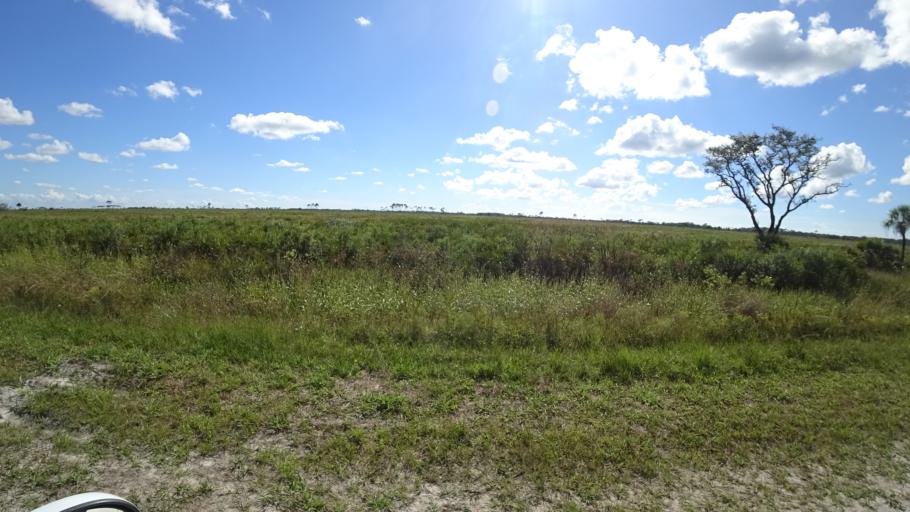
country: US
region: Florida
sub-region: Sarasota County
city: Lake Sarasota
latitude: 27.2446
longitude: -82.2714
